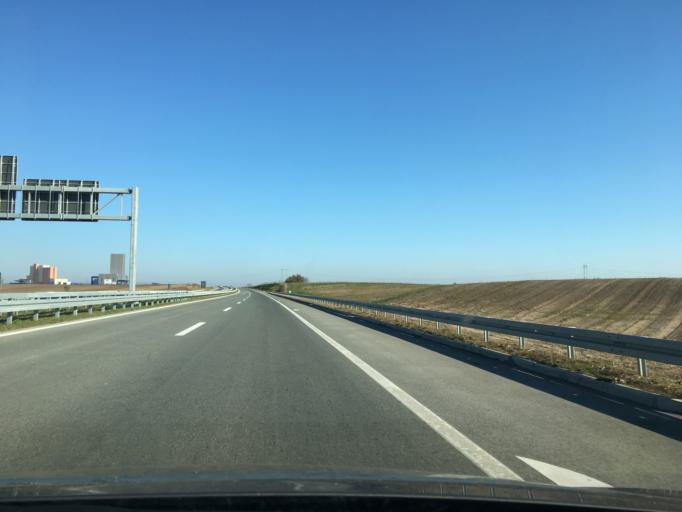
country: RS
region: Autonomna Pokrajina Vojvodina
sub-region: Severnobacki Okrug
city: Mali Igos
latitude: 45.6489
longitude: 19.7193
